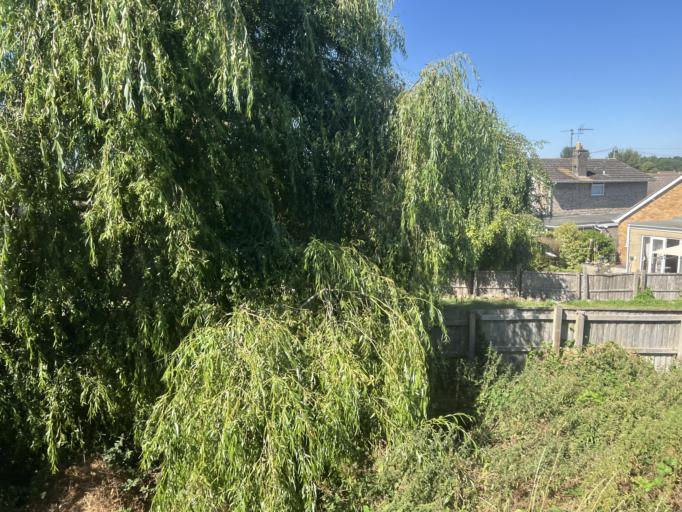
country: GB
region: England
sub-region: Lincolnshire
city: Boston
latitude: 52.9870
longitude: -0.0333
